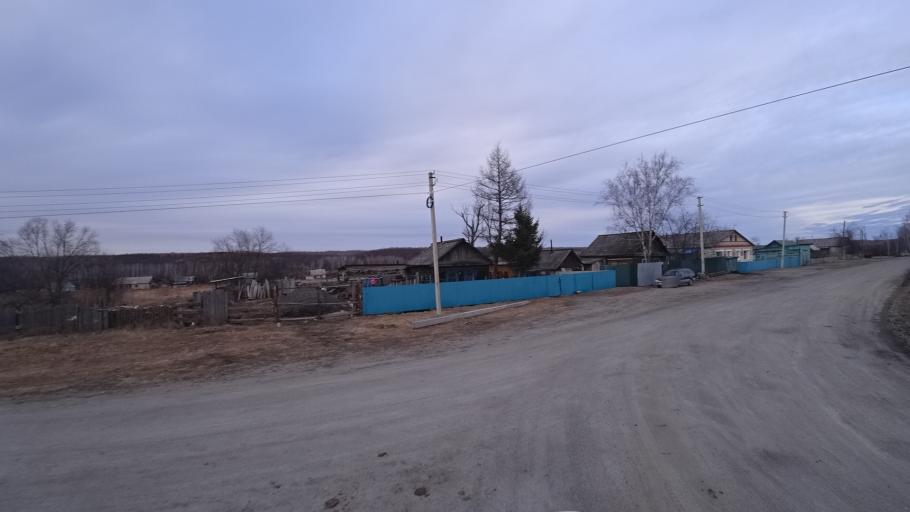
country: RU
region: Amur
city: Bureya
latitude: 50.0200
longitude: 129.7688
